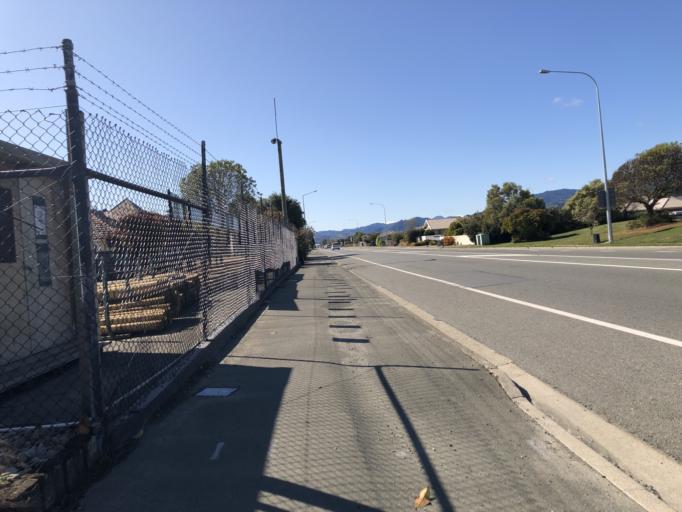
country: NZ
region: Tasman
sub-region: Tasman District
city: Richmond
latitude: -41.3437
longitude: 173.1702
